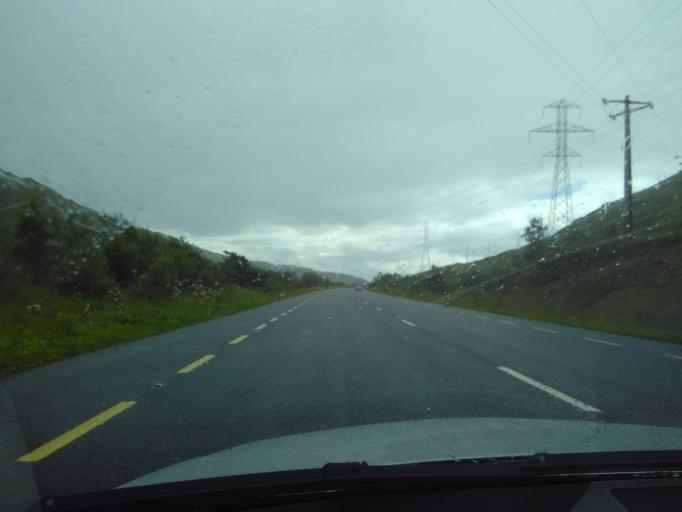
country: IE
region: Ulster
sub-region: County Donegal
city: Donegal
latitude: 54.7162
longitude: -7.9606
